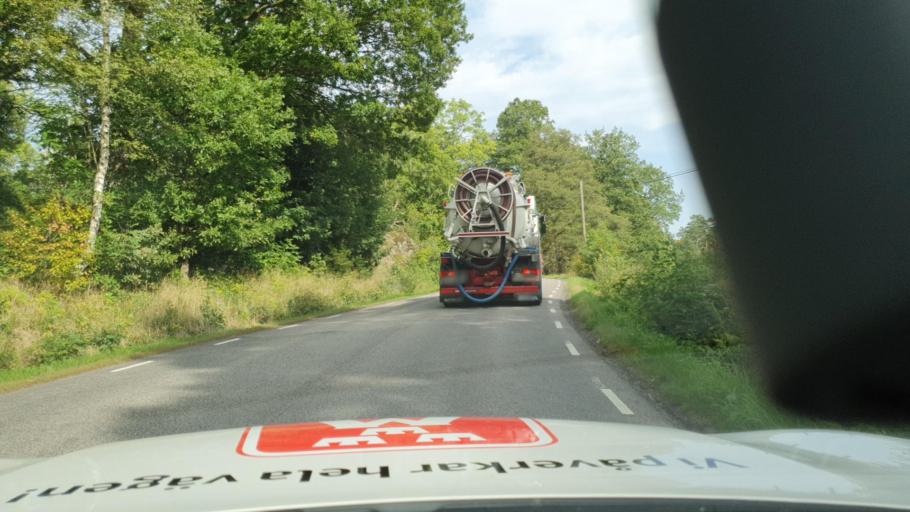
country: SE
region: Vaestra Goetaland
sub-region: Marks Kommun
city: Kinna
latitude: 57.4484
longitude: 12.6920
